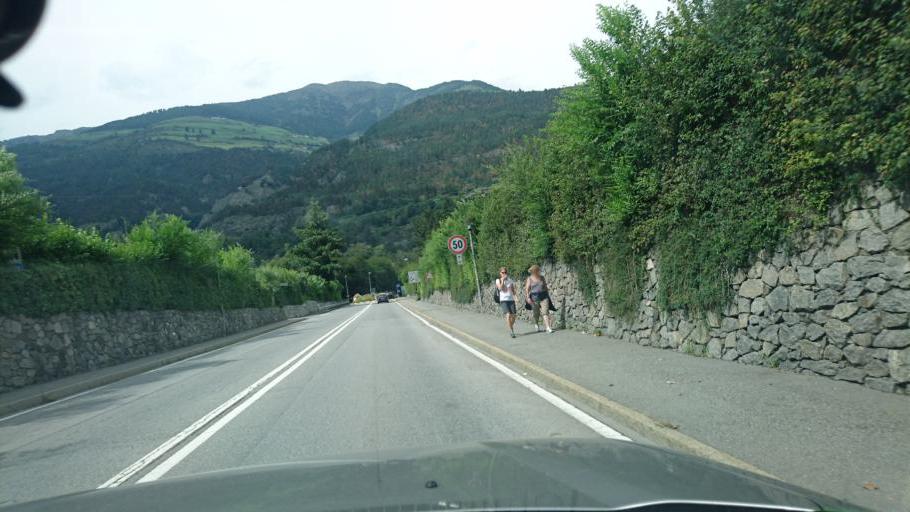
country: IT
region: Trentino-Alto Adige
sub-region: Bolzano
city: Silandro
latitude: 46.6266
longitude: 10.7703
